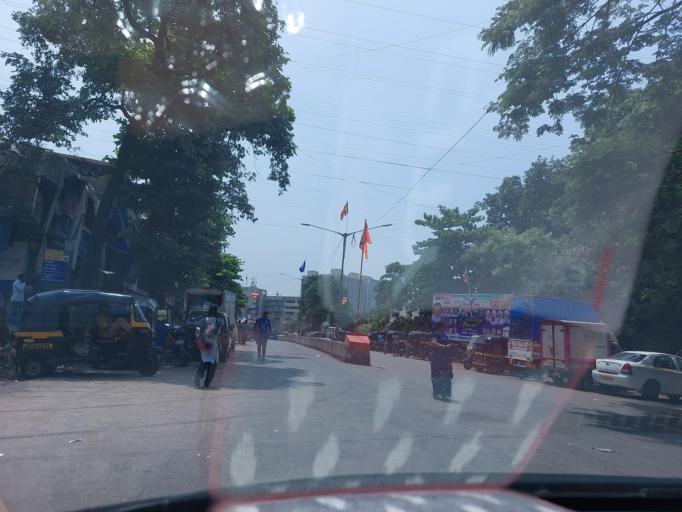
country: IN
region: Maharashtra
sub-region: Mumbai Suburban
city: Mumbai
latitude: 19.0561
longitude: 72.8839
